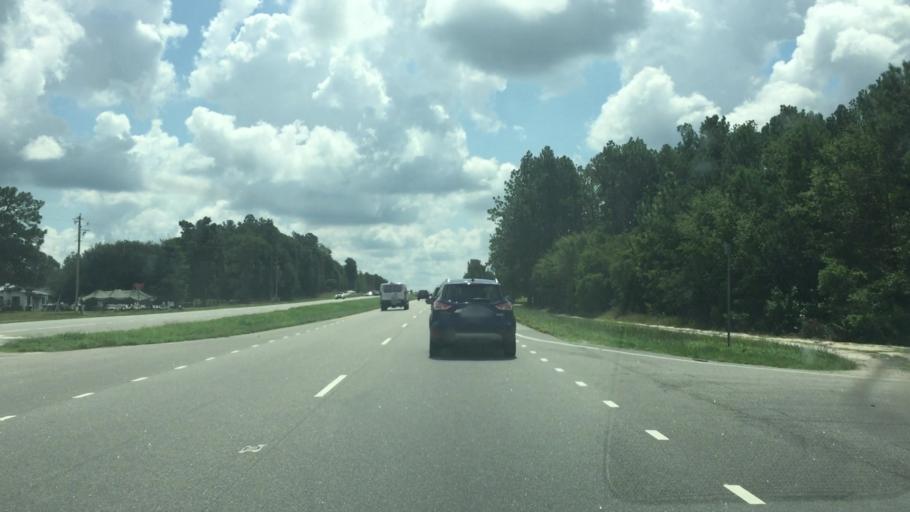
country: US
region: North Carolina
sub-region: Scotland County
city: Laurel Hill
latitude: 34.8443
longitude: -79.6086
